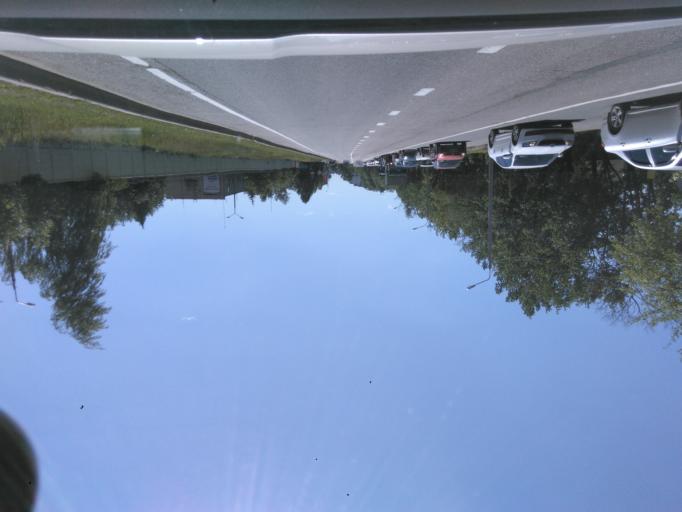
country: RU
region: Moskovskaya
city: Solnechnogorsk
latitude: 56.1798
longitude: 36.9548
